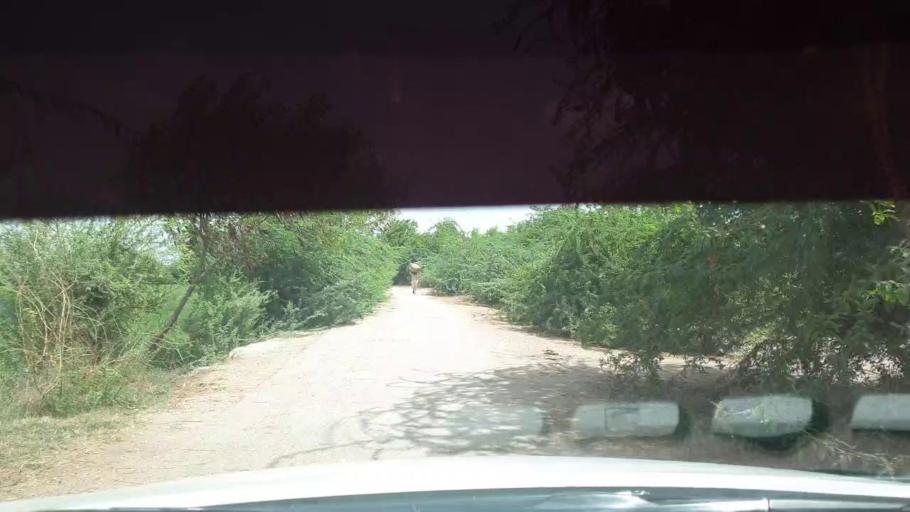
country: PK
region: Sindh
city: Kadhan
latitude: 24.5053
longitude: 68.9798
